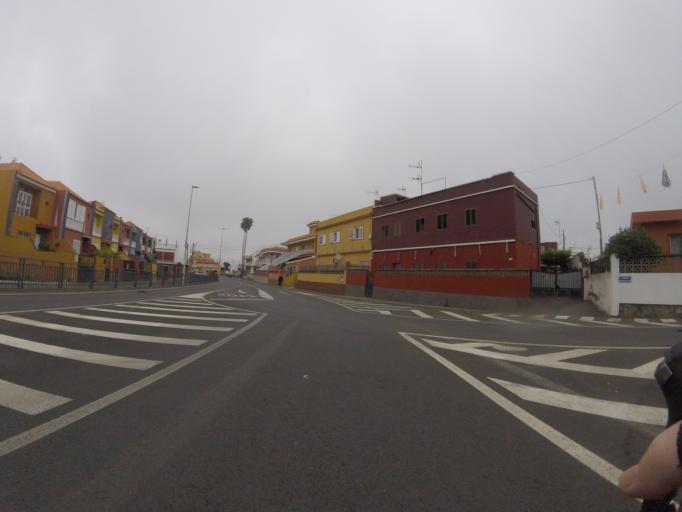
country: ES
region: Canary Islands
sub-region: Provincia de Santa Cruz de Tenerife
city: Tacoronte
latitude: 28.4954
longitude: -16.3768
